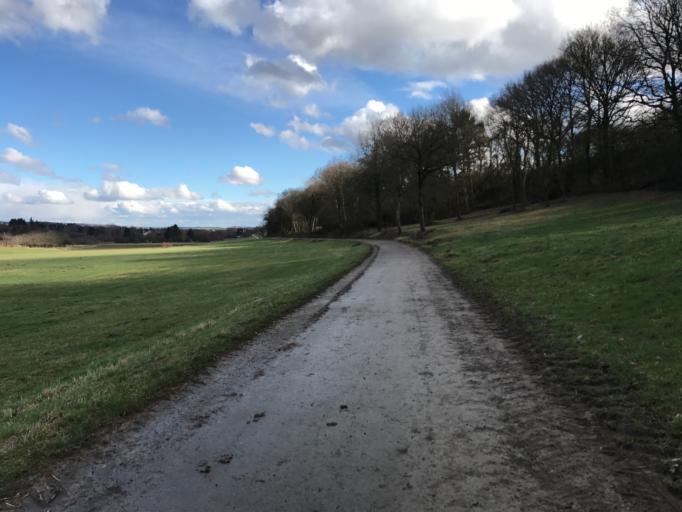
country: DE
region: Hesse
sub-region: Regierungsbezirk Darmstadt
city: Wiesbaden
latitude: 50.1000
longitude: 8.2882
